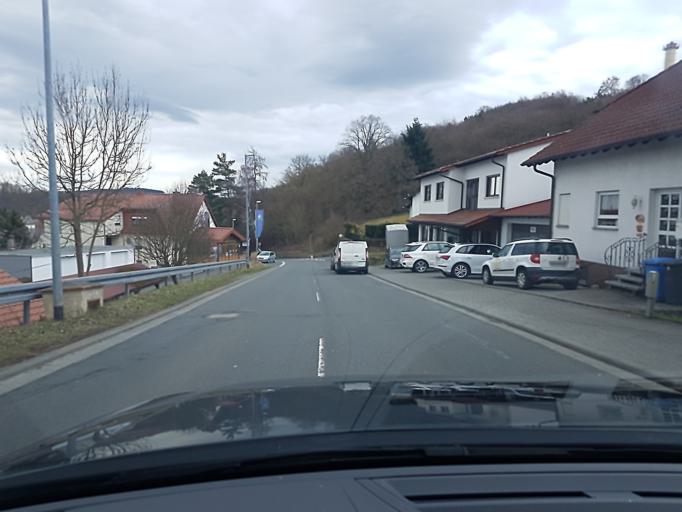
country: DE
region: Hesse
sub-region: Regierungsbezirk Giessen
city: Merkenbach
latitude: 50.6541
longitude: 8.2965
